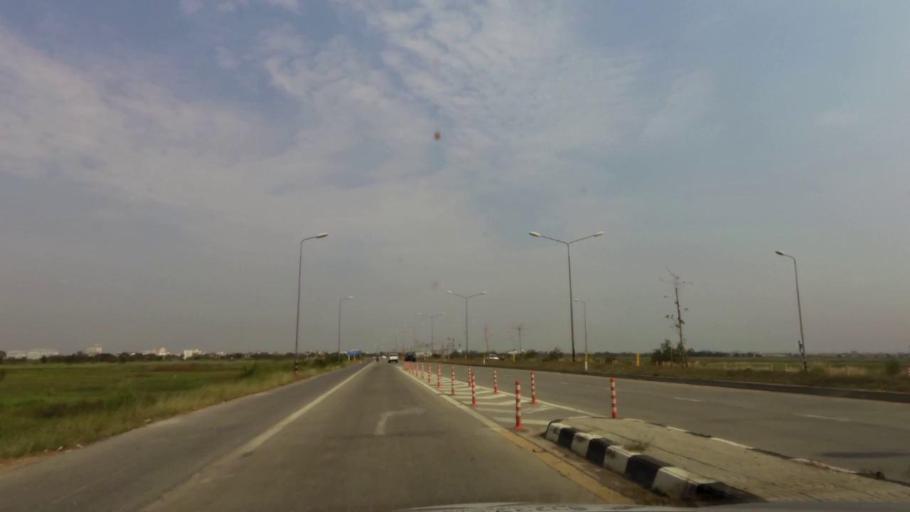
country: TH
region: Phra Nakhon Si Ayutthaya
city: Phra Nakhon Si Ayutthaya
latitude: 14.3310
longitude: 100.5883
